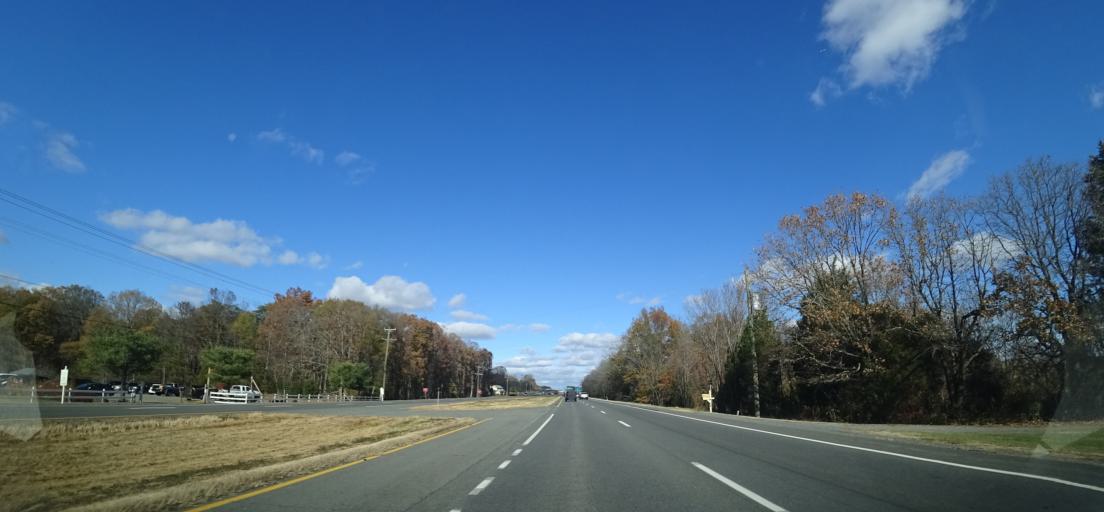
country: US
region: Virginia
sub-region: Fauquier County
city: Bealeton
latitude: 38.6037
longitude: -77.8002
